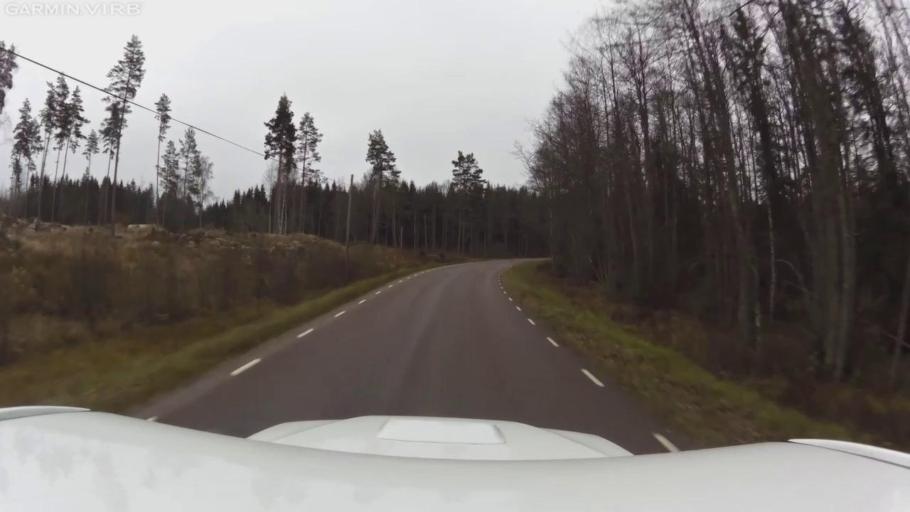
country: SE
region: OEstergoetland
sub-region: Linkopings Kommun
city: Vikingstad
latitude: 58.2392
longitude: 15.3901
